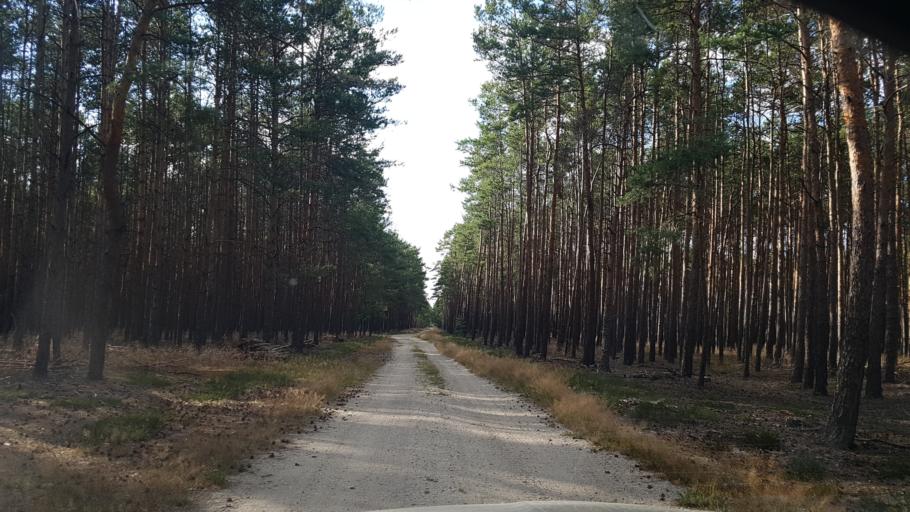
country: DE
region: Brandenburg
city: Trobitz
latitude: 51.6289
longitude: 13.4084
